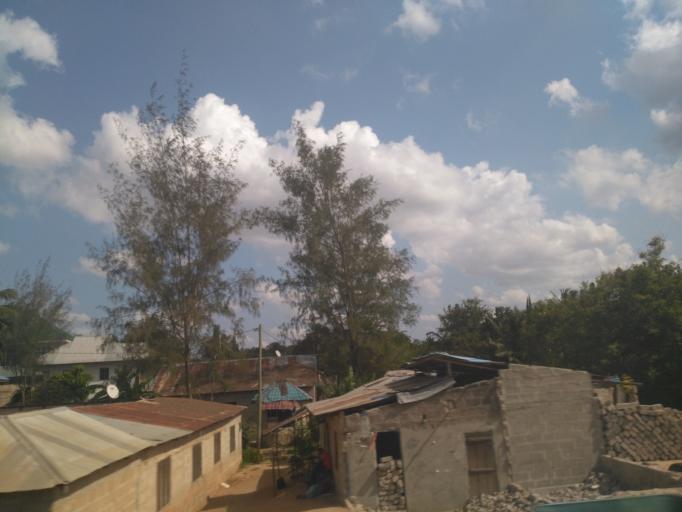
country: TZ
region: Dar es Salaam
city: Dar es Salaam
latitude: -6.8951
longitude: 39.2749
